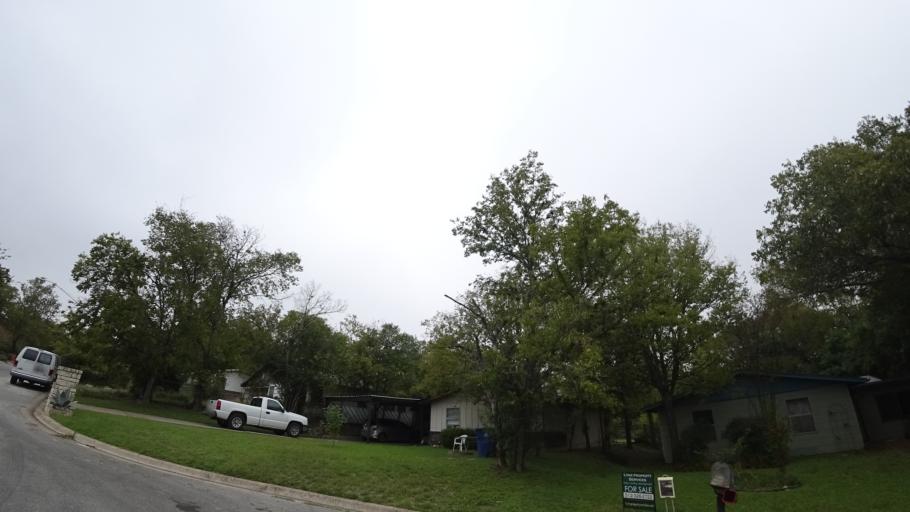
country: US
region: Texas
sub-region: Travis County
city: Austin
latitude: 30.2183
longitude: -97.7727
